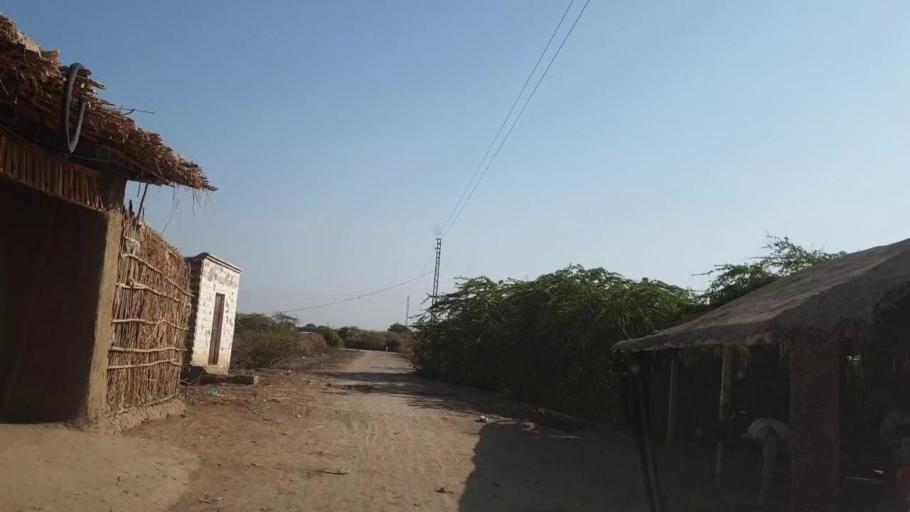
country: PK
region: Sindh
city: Naukot
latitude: 25.0308
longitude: 69.4467
